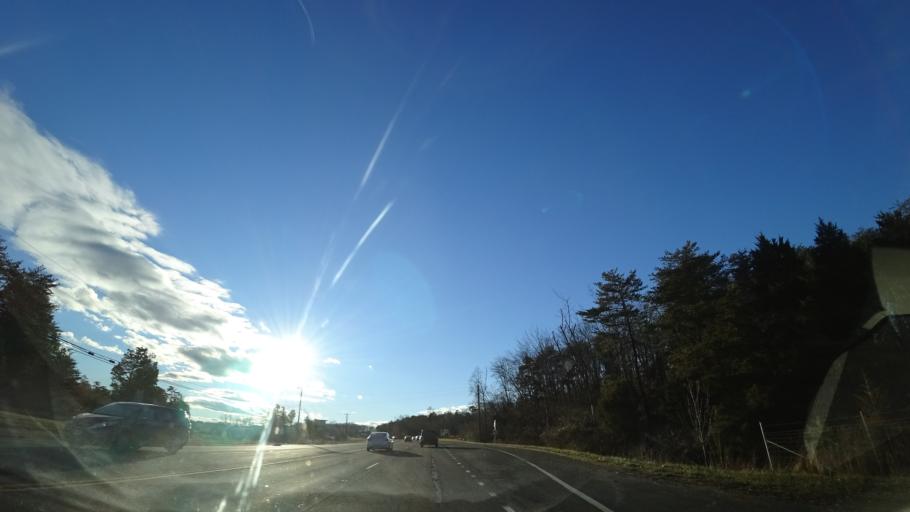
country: US
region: Virginia
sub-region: Prince William County
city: Linton Hall
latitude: 38.7352
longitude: -77.5413
